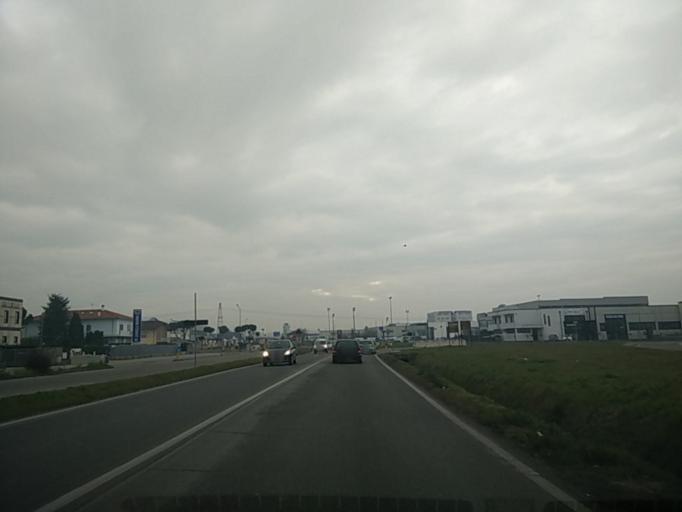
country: IT
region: Emilia-Romagna
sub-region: Provincia di Rimini
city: Santa Giustina
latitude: 44.0676
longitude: 12.4706
